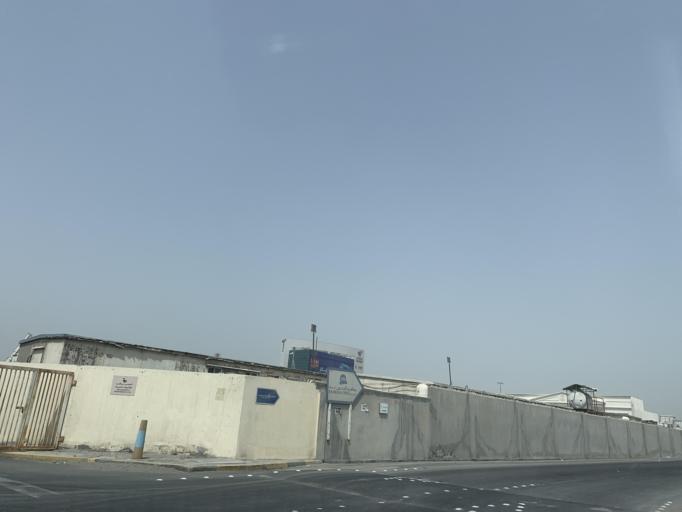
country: BH
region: Northern
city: Madinat `Isa
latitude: 26.1880
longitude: 50.5345
